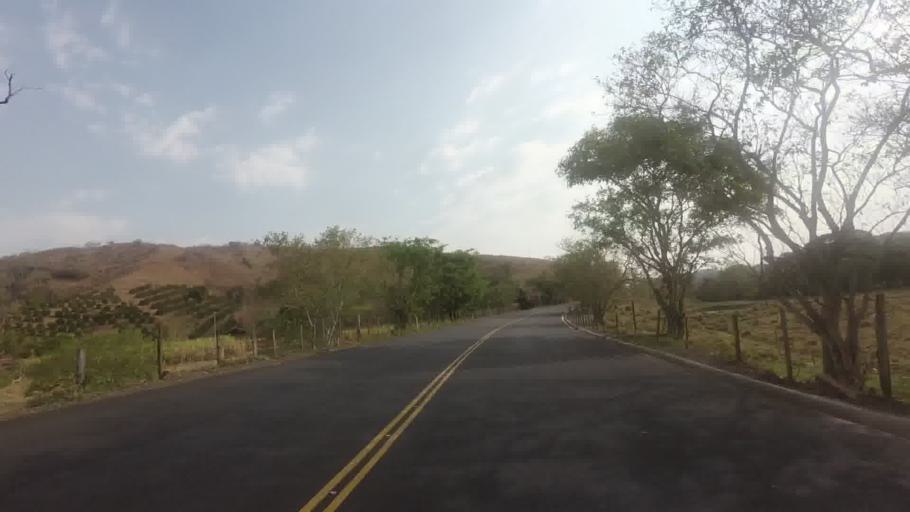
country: BR
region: Rio de Janeiro
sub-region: Itaperuna
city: Itaperuna
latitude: -21.3113
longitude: -41.8575
